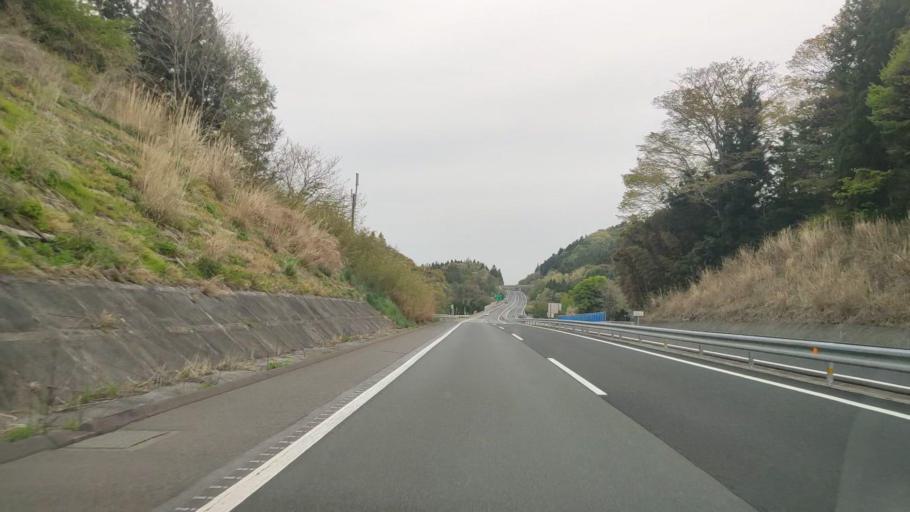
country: JP
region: Fukushima
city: Funehikimachi-funehiki
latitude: 37.2778
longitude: 140.6297
